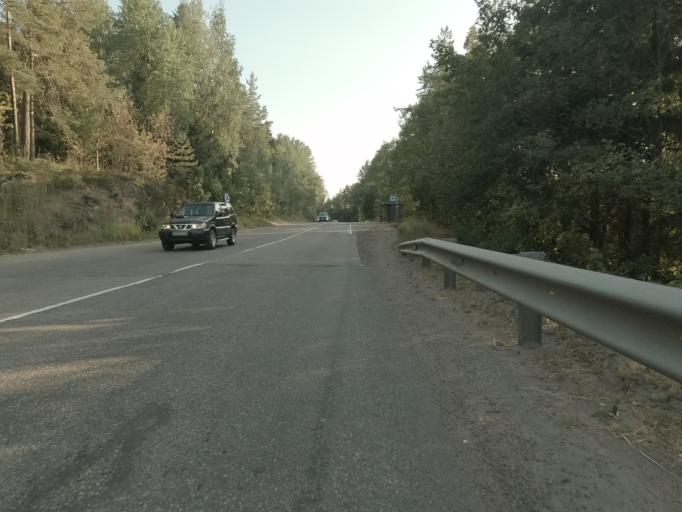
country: RU
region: Leningrad
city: Vyborg
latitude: 60.7396
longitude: 28.7617
